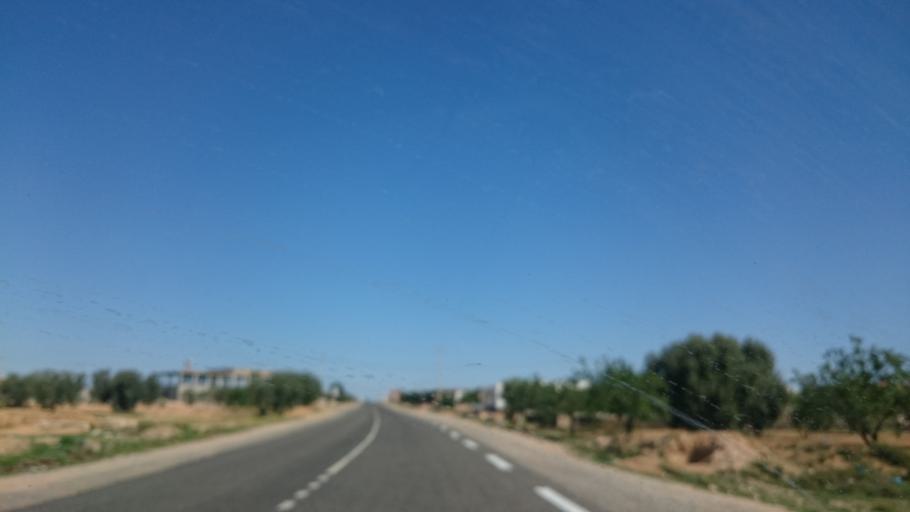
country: TN
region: Safaqis
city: Sfax
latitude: 34.7755
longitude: 10.5070
